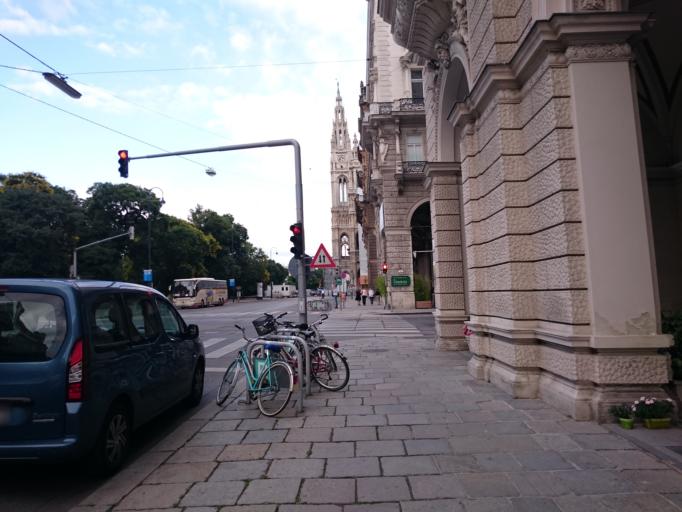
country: AT
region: Vienna
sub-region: Wien Stadt
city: Vienna
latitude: 48.2127
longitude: 16.3590
